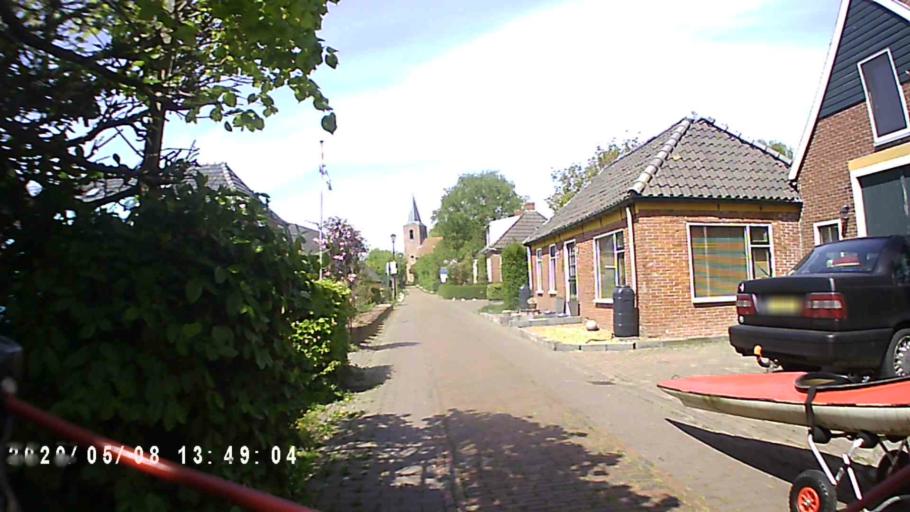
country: NL
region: Groningen
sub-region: Gemeente Appingedam
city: Appingedam
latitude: 53.3386
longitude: 6.7805
